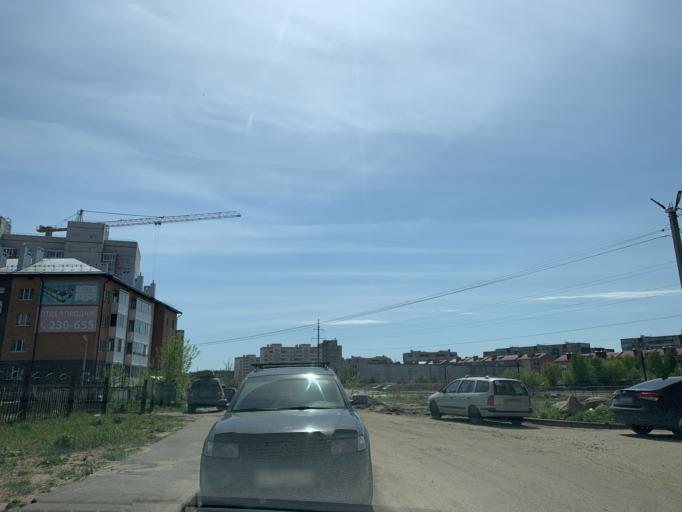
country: RU
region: Jaroslavl
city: Yaroslavl
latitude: 57.6545
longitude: 39.9683
